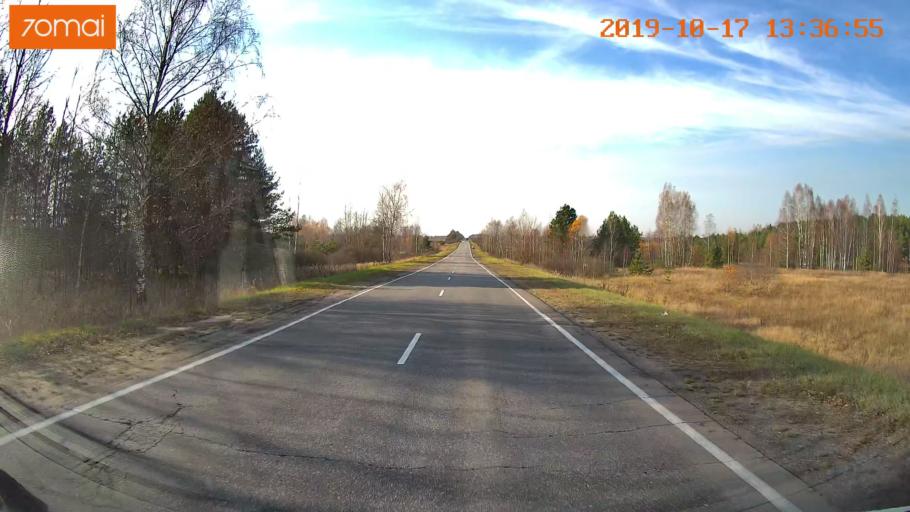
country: RU
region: Rjazan
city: Tuma
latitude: 55.1404
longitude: 40.6513
